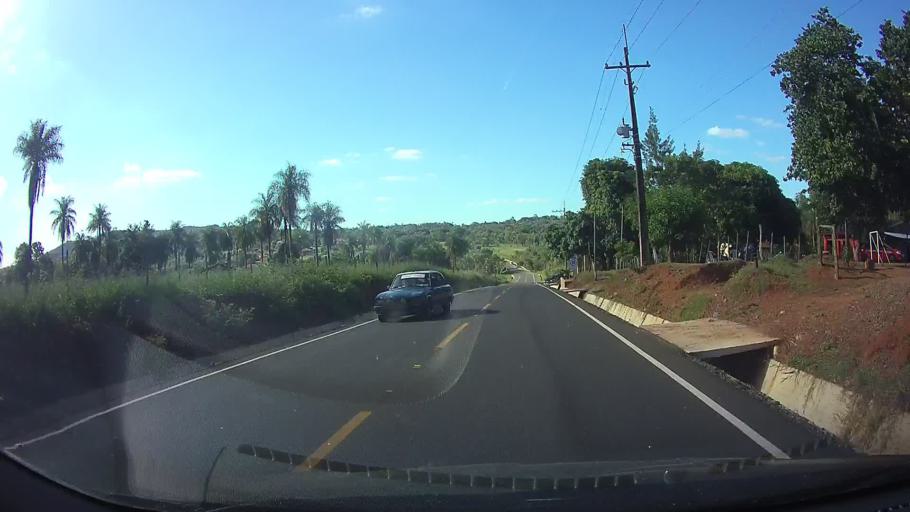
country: PY
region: Cordillera
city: Caacupe
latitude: -25.3575
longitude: -57.1469
